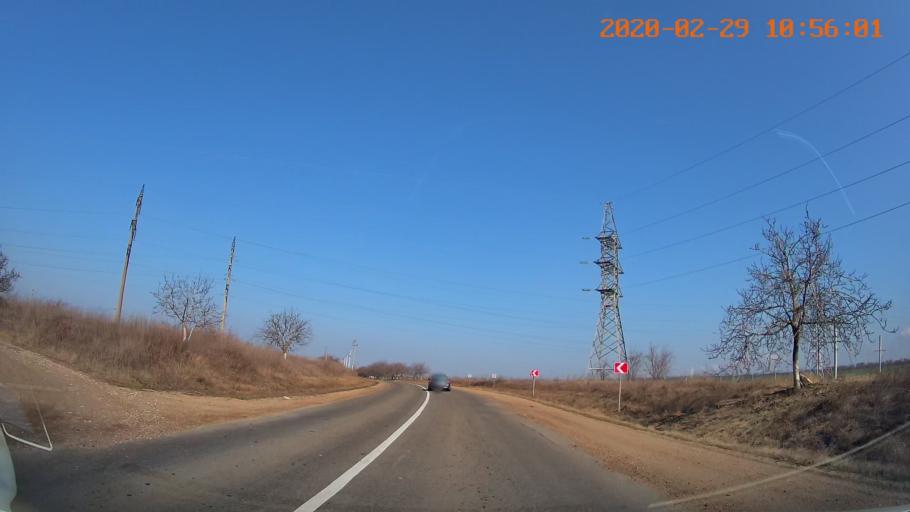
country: MD
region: Telenesti
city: Grigoriopol
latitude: 47.1406
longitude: 29.3258
